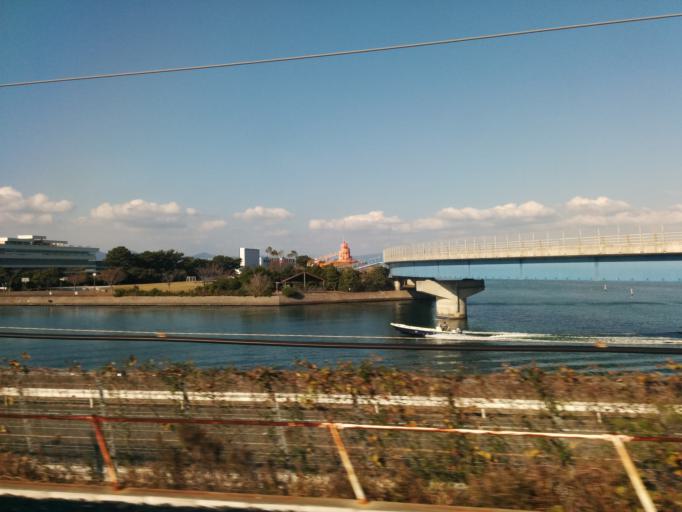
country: JP
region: Shizuoka
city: Kosai-shi
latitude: 34.6946
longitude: 137.5760
